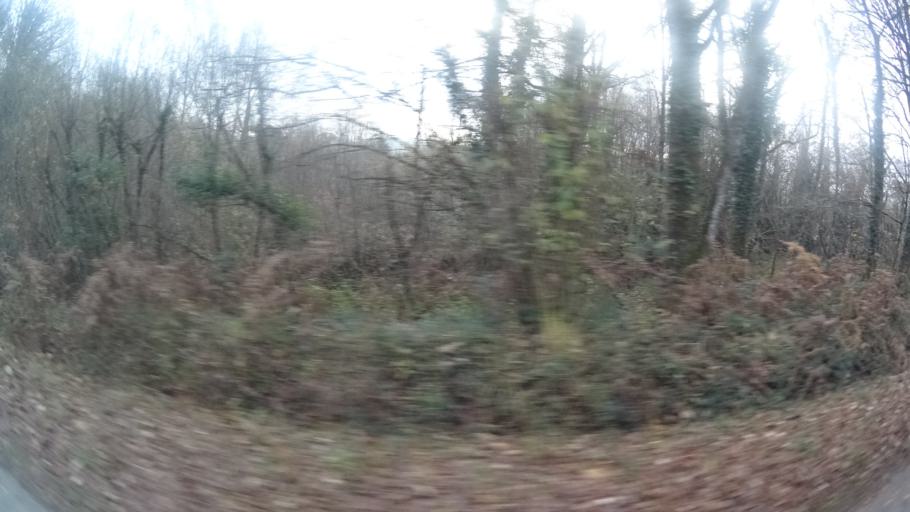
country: FR
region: Pays de la Loire
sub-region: Departement de la Loire-Atlantique
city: Avessac
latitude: 47.6523
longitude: -2.0130
